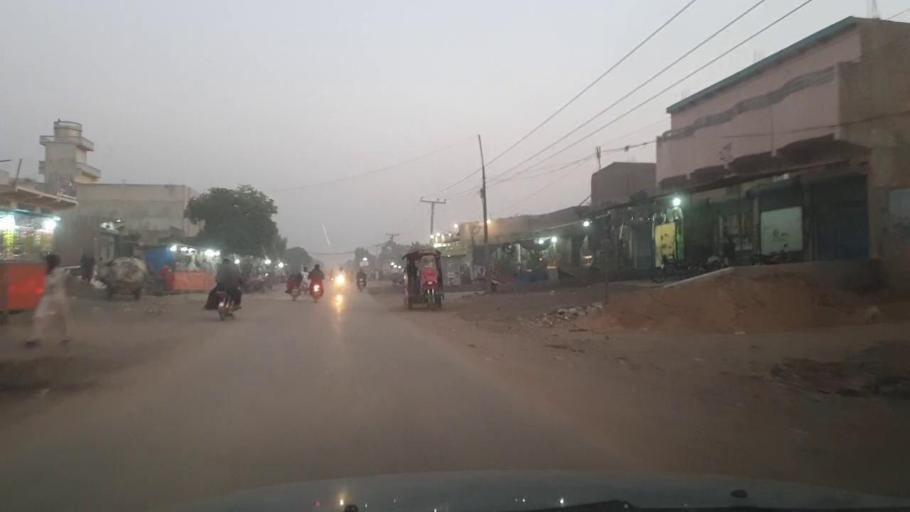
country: PK
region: Sindh
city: Tando Allahyar
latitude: 25.4519
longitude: 68.7247
